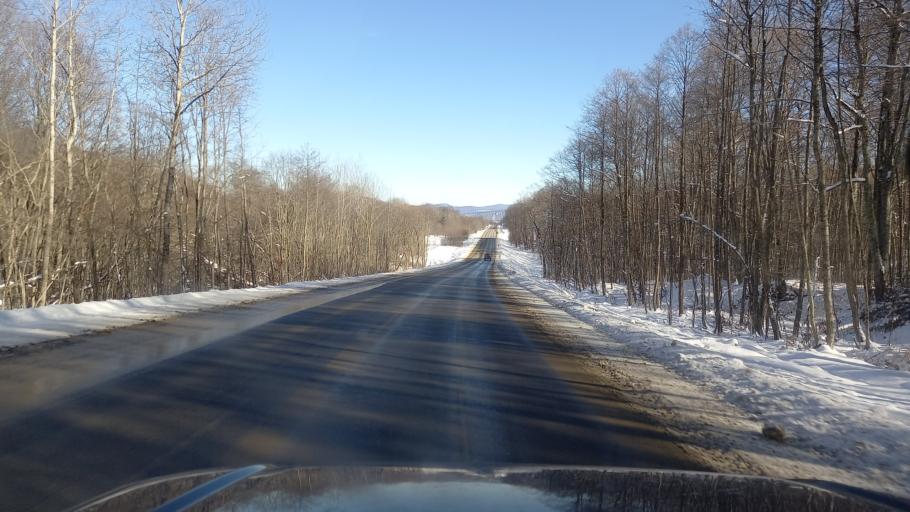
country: RU
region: Adygeya
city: Kamennomostskiy
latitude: 44.2178
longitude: 40.0802
